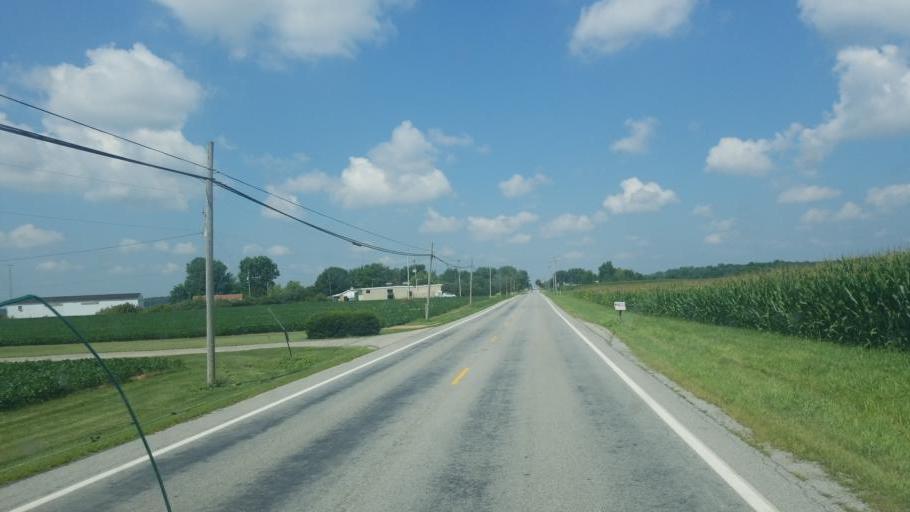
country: US
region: Ohio
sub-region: Allen County
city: Lima
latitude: 40.7122
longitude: -84.0182
